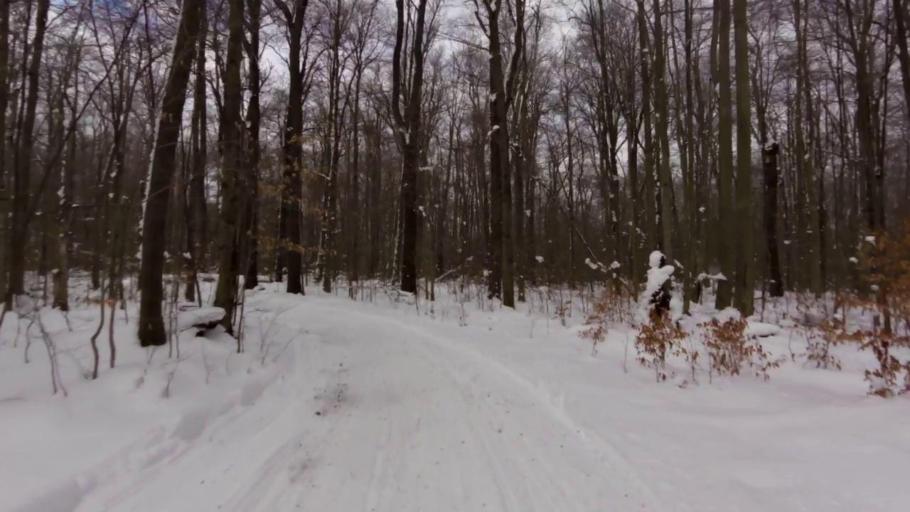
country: US
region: Pennsylvania
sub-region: McKean County
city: Bradford
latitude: 42.0302
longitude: -78.7406
